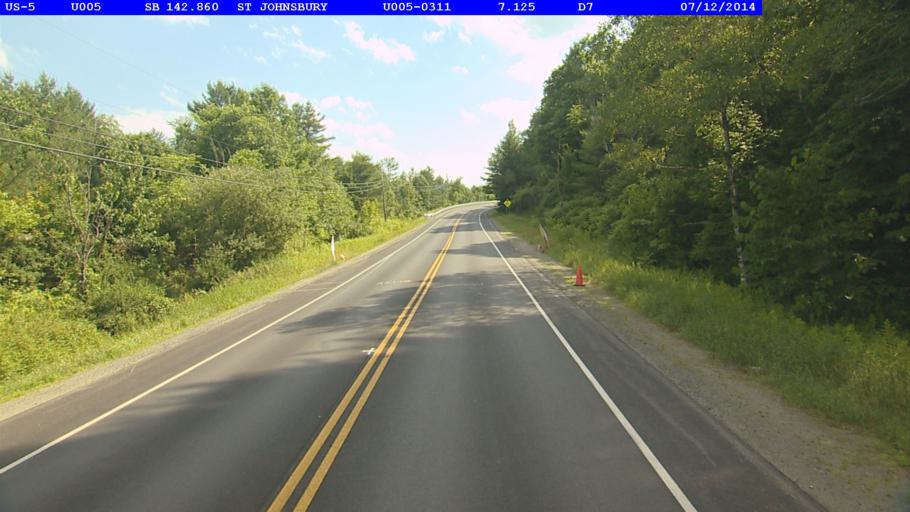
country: US
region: Vermont
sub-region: Caledonia County
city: Lyndon
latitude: 44.4907
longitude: -72.0059
